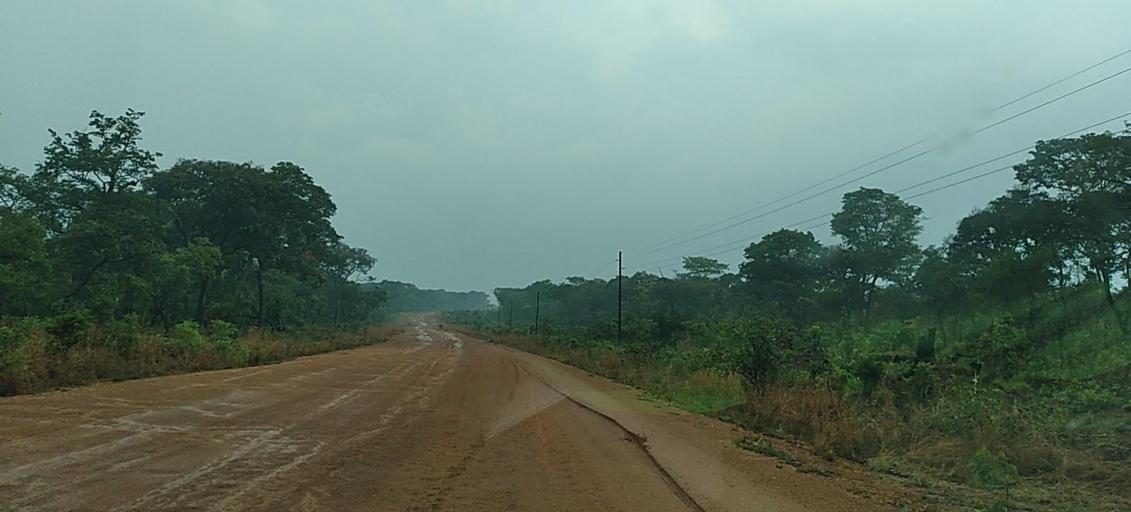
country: ZM
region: North-Western
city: Mwinilunga
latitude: -11.5946
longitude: 24.3899
